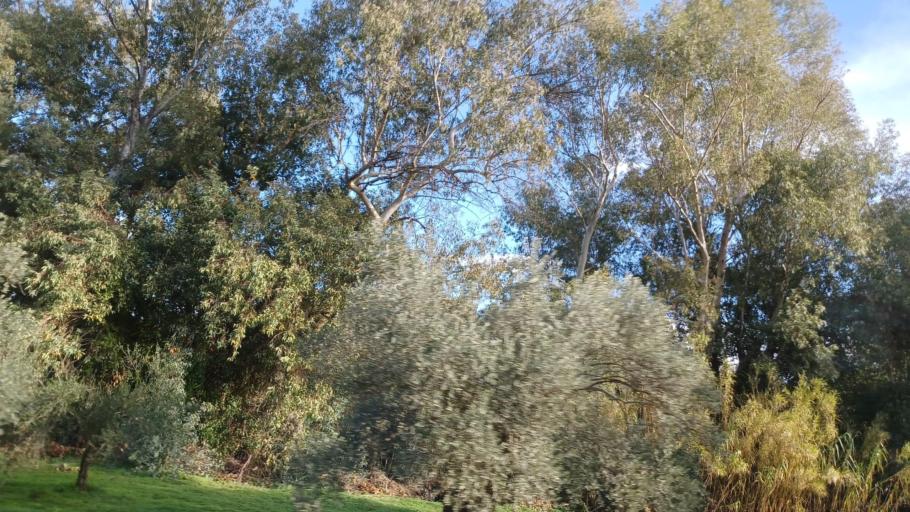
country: CY
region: Lefkosia
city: Lythrodontas
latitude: 34.9336
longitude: 33.2979
